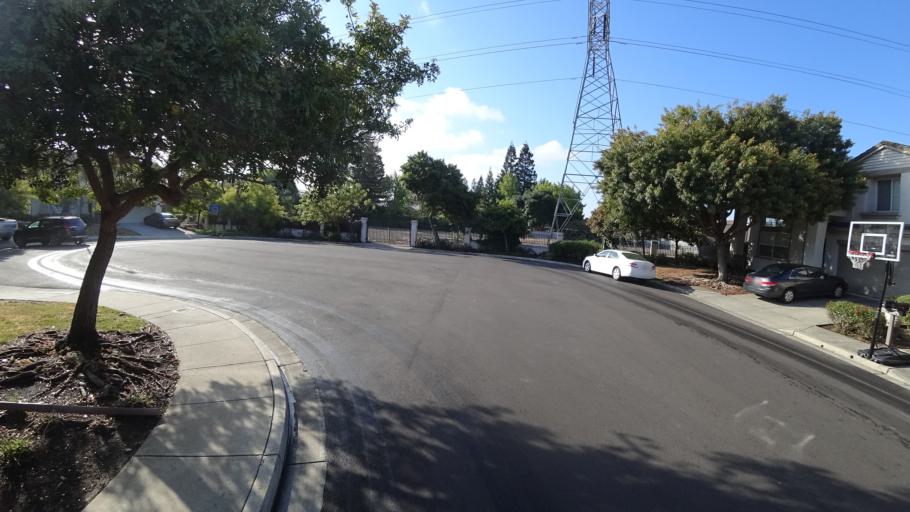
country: US
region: California
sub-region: Alameda County
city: Hayward
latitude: 37.6515
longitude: -122.0822
